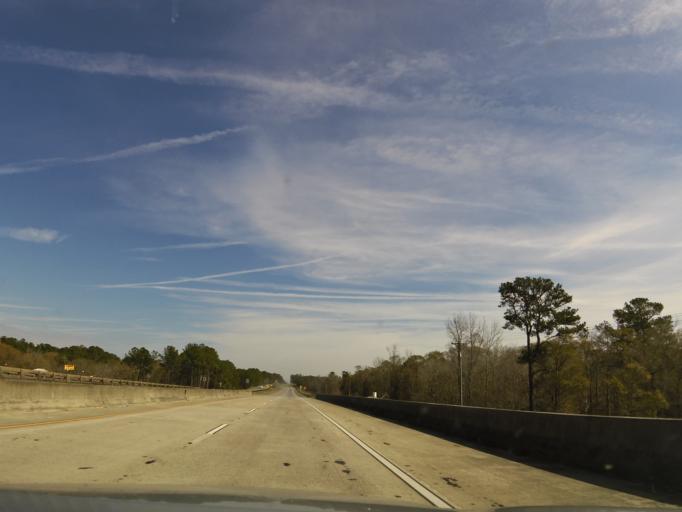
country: US
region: Georgia
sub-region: Brantley County
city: Nahunta
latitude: 31.2196
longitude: -81.8668
